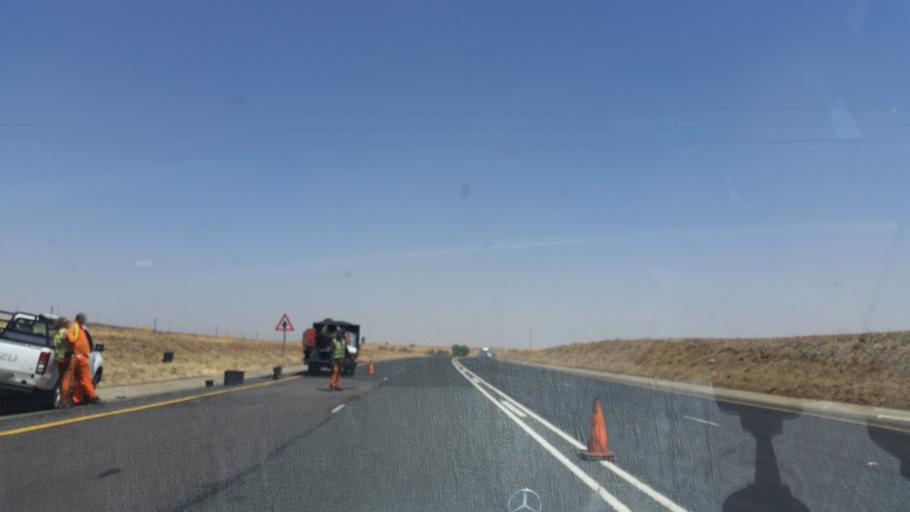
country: ZA
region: Orange Free State
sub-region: Lejweleputswa District Municipality
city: Brandfort
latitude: -28.8136
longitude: 26.6711
